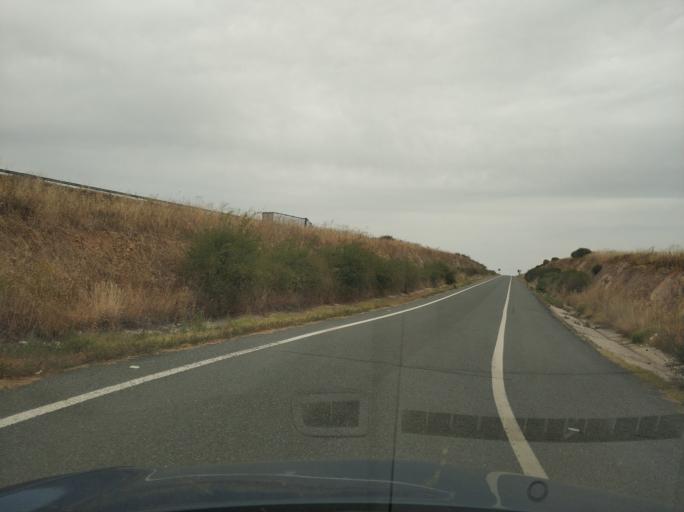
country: ES
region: Castille and Leon
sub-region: Provincia de Salamanca
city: Buenavista
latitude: 40.7684
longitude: -5.6268
